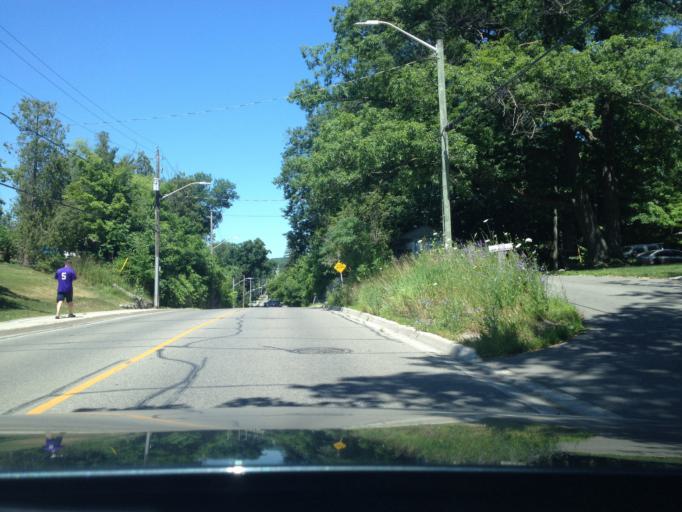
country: CA
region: Ontario
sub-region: Halton
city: Milton
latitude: 43.6623
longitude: -79.9195
